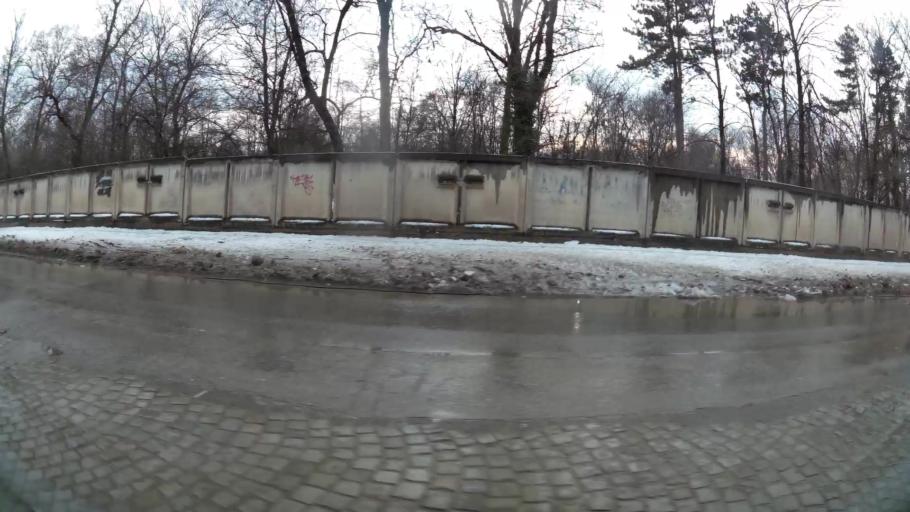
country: BG
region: Sofia-Capital
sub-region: Stolichna Obshtina
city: Sofia
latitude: 42.7191
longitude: 23.3362
